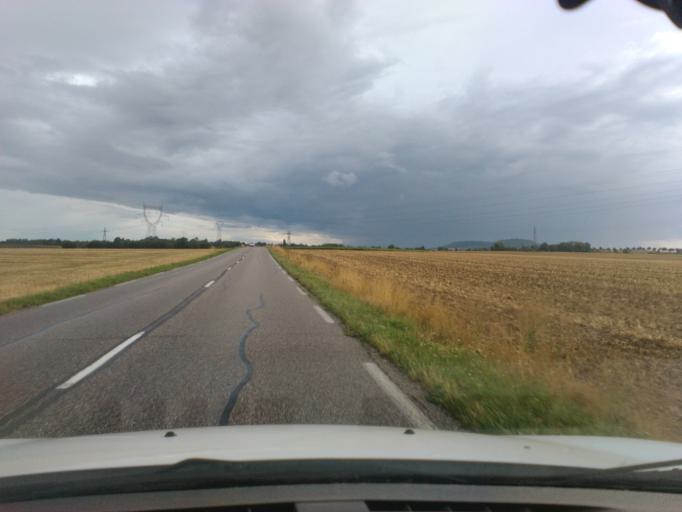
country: FR
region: Lorraine
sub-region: Departement de Meurthe-et-Moselle
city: Vezelise
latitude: 48.4836
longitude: 6.1427
